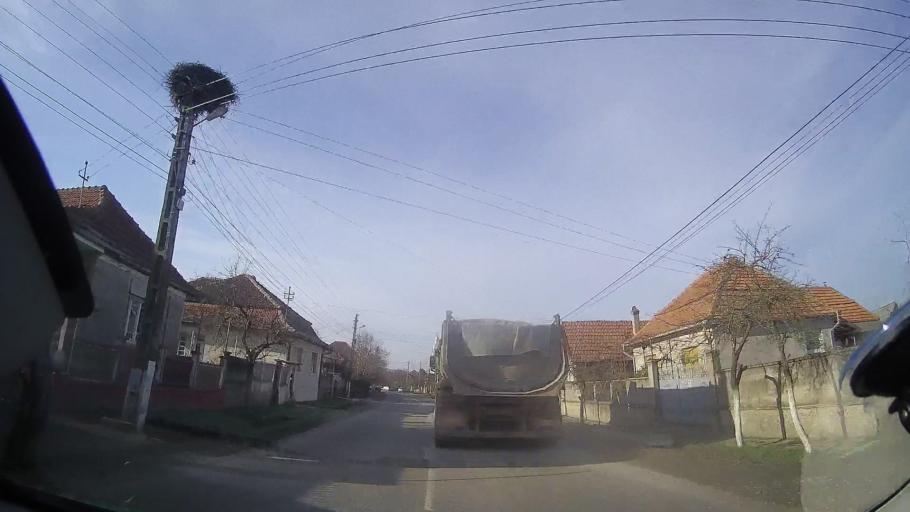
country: RO
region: Bihor
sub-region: Comuna Brusturi
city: Brusturi
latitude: 47.1422
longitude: 22.2639
